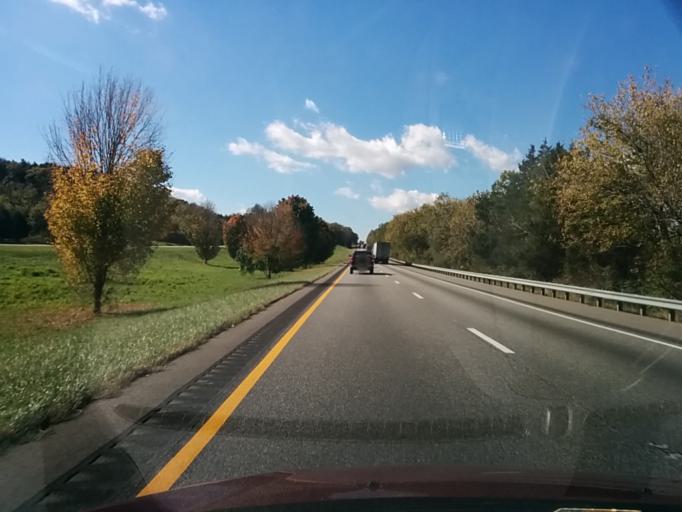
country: US
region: Virginia
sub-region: Botetourt County
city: Buchanan
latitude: 37.4891
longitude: -79.7699
